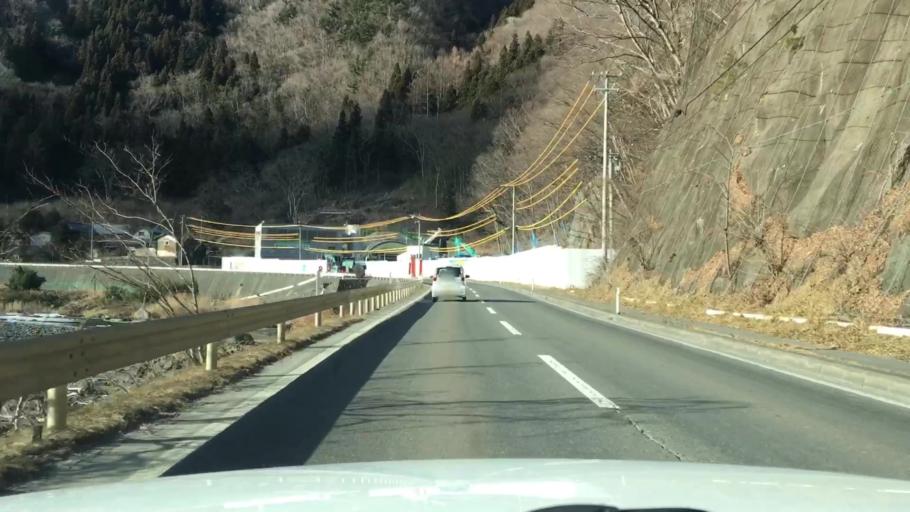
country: JP
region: Iwate
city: Miyako
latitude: 39.6042
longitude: 141.6984
